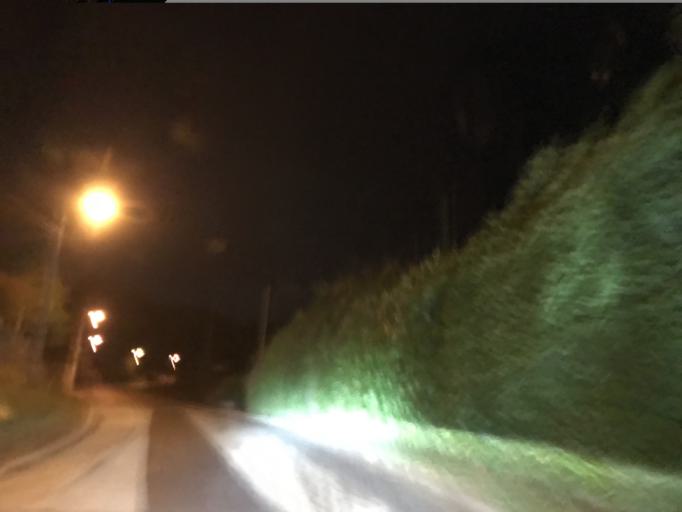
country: FR
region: Auvergne
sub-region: Departement du Puy-de-Dome
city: Thiers
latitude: 45.8451
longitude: 3.5447
